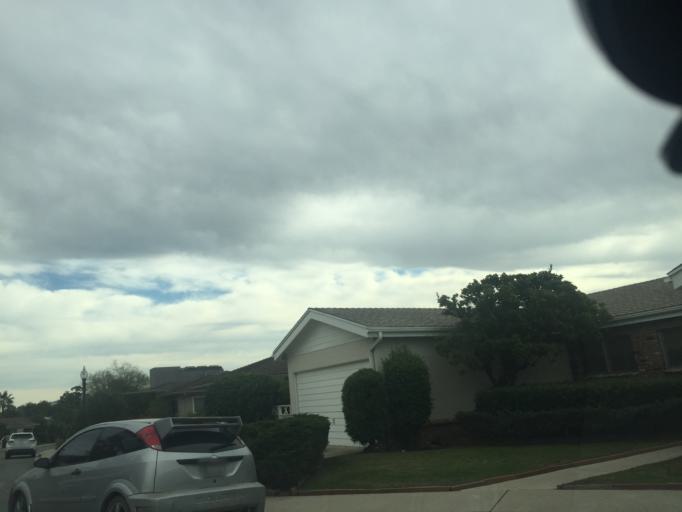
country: US
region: California
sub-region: San Diego County
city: Lemon Grove
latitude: 32.7701
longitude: -117.0950
